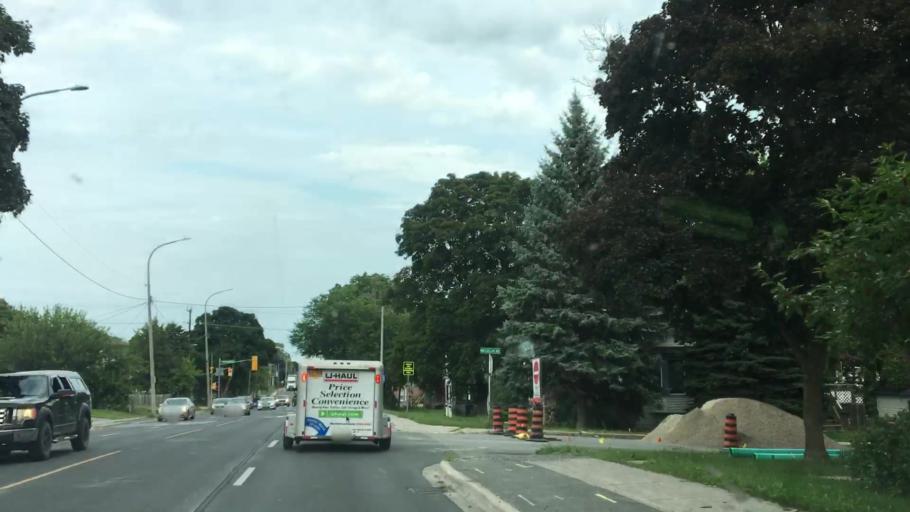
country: CA
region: Ontario
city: Quinte West
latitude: 44.0979
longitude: -77.5843
